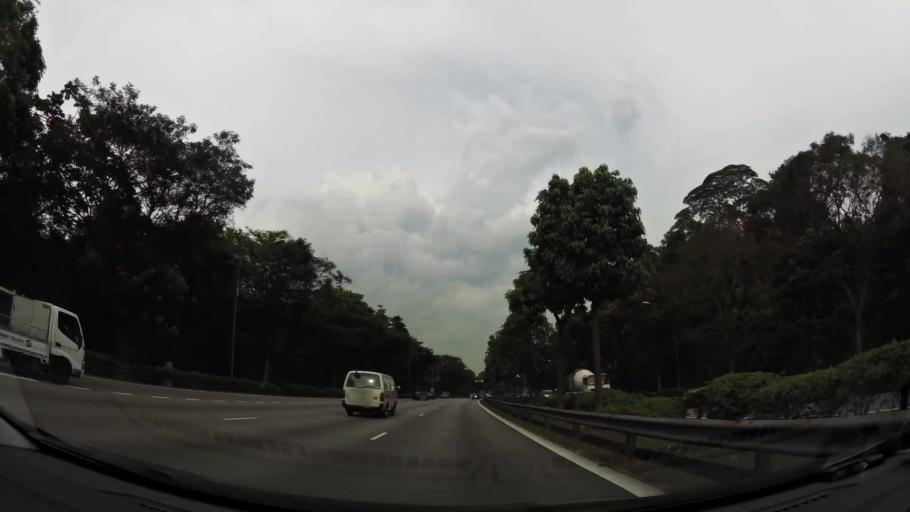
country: MY
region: Johor
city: Johor Bahru
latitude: 1.4248
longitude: 103.7757
